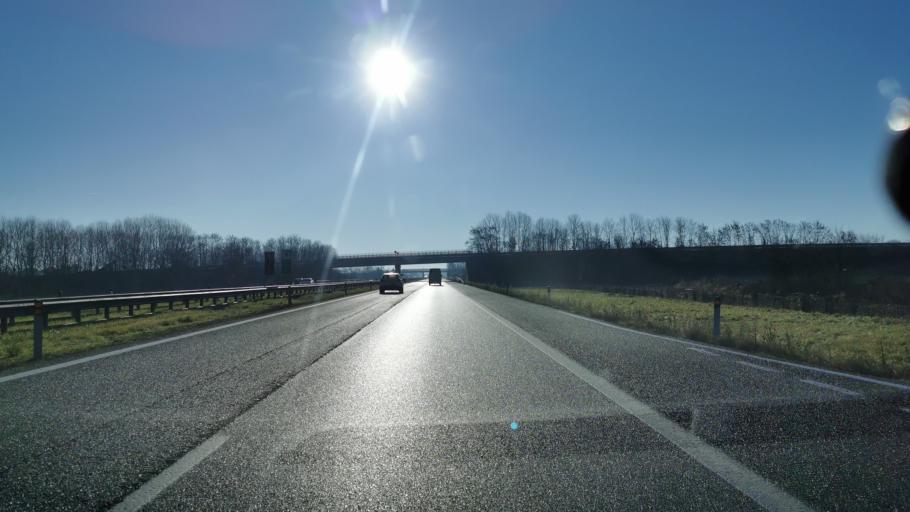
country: IT
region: Piedmont
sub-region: Provincia di Torino
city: Villastellone
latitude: 44.9244
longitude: 7.7304
